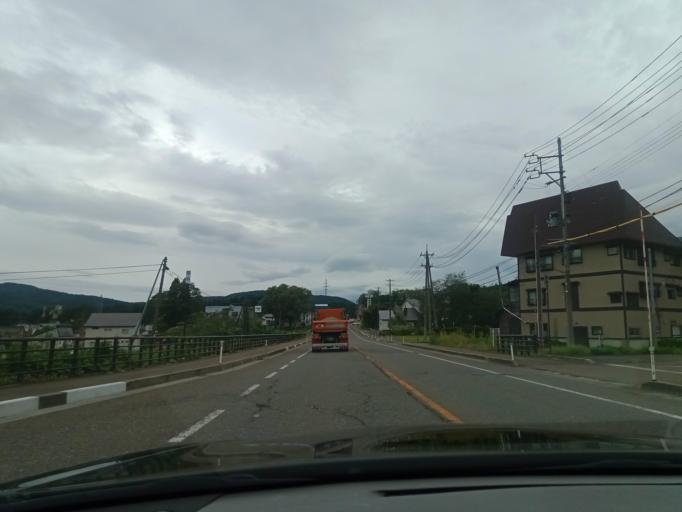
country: JP
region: Niigata
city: Arai
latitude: 36.8822
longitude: 138.2054
